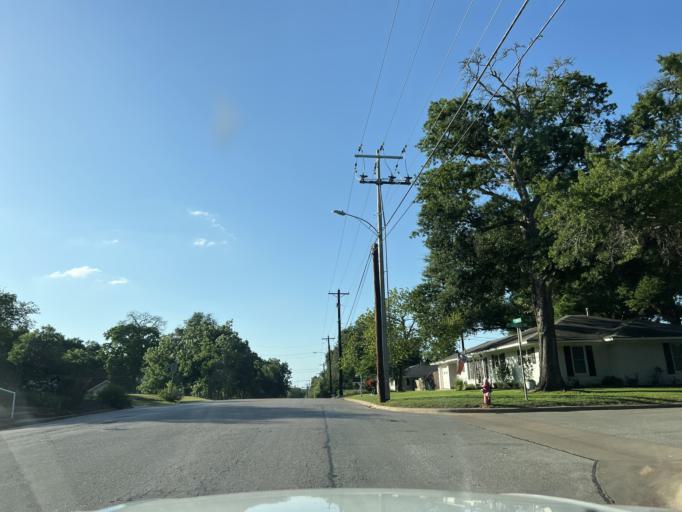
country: US
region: Texas
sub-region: Washington County
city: Brenham
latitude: 30.1571
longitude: -96.3867
